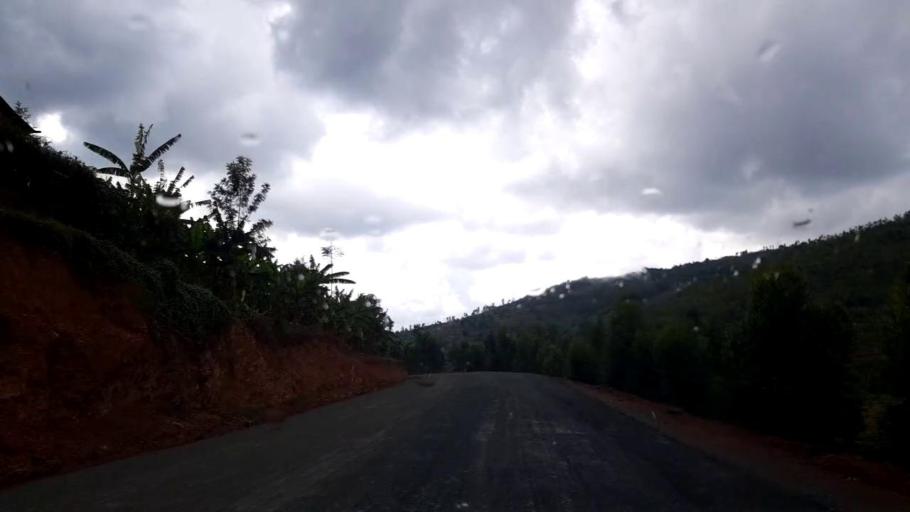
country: RW
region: Northern Province
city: Byumba
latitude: -1.6093
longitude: 30.2346
